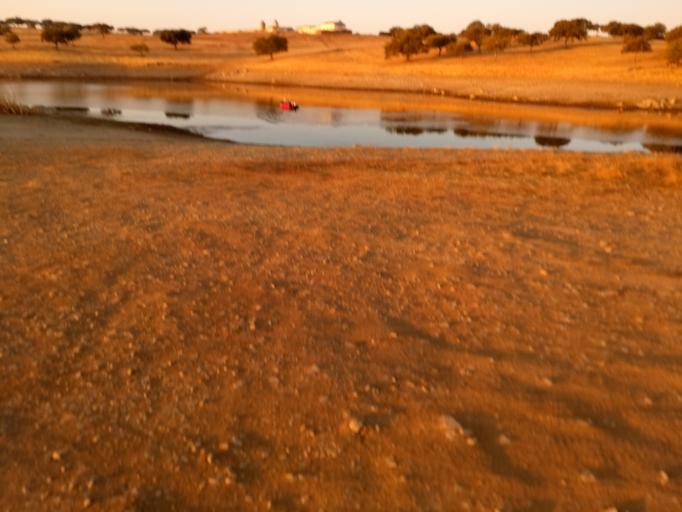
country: PT
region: Evora
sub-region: Mourao
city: Mourao
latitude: 38.3548
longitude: -7.4443
